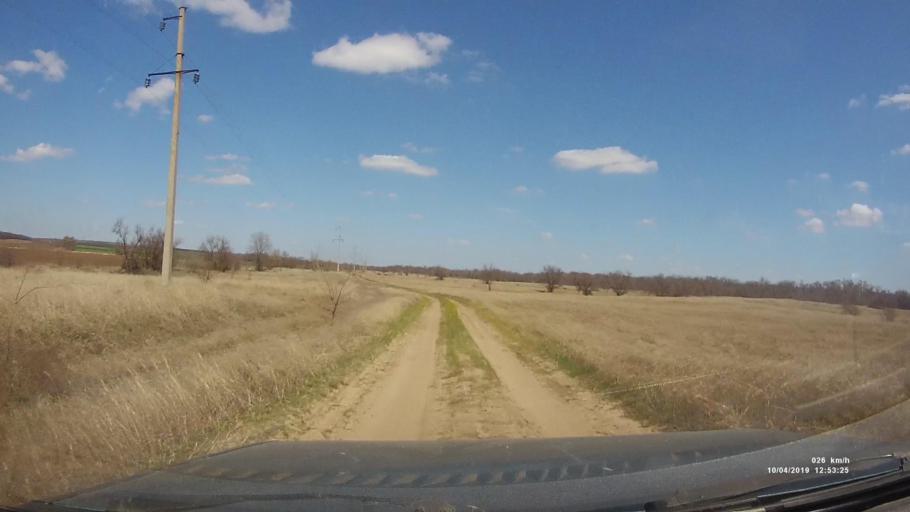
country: RU
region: Rostov
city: Masalovka
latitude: 48.3641
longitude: 40.2210
